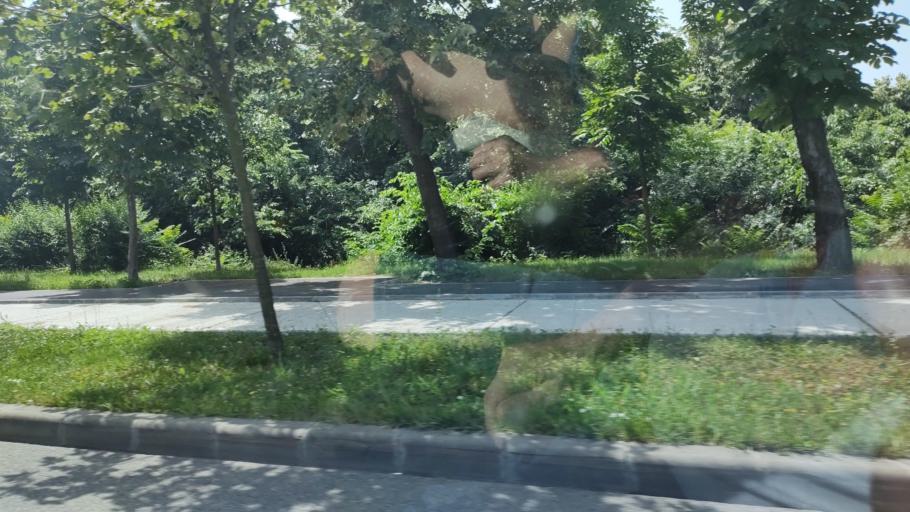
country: RO
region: Mehedinti
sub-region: Municipiul Drobeta-Turnu Severin
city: Drobeta-Turnu Severin
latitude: 44.6230
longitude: 22.6447
